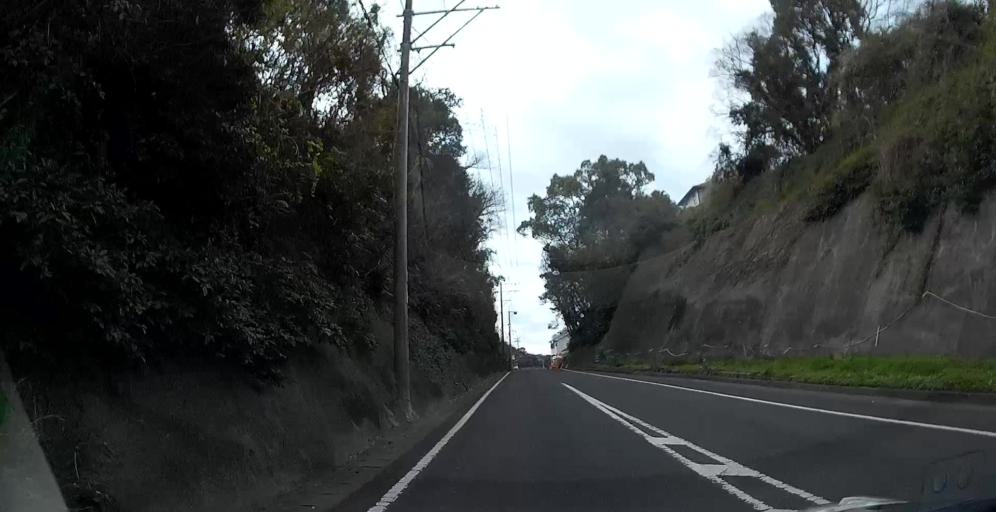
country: JP
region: Kumamoto
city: Minamata
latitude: 32.2104
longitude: 130.3851
